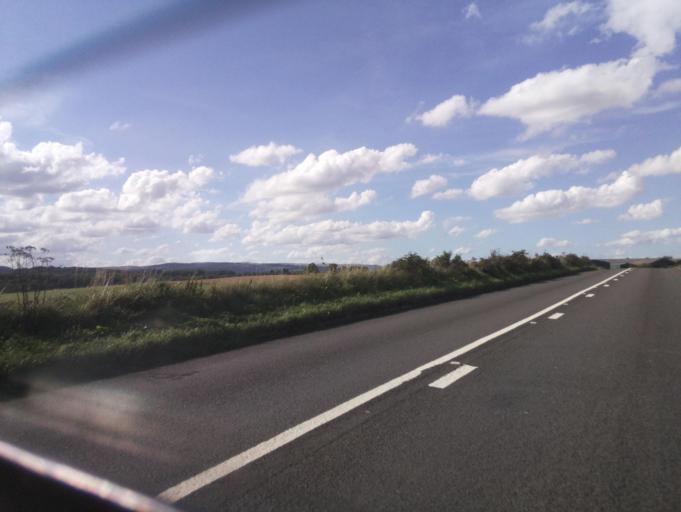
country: GB
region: Scotland
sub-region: Stirling
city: Plean
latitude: 56.0772
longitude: -3.8928
